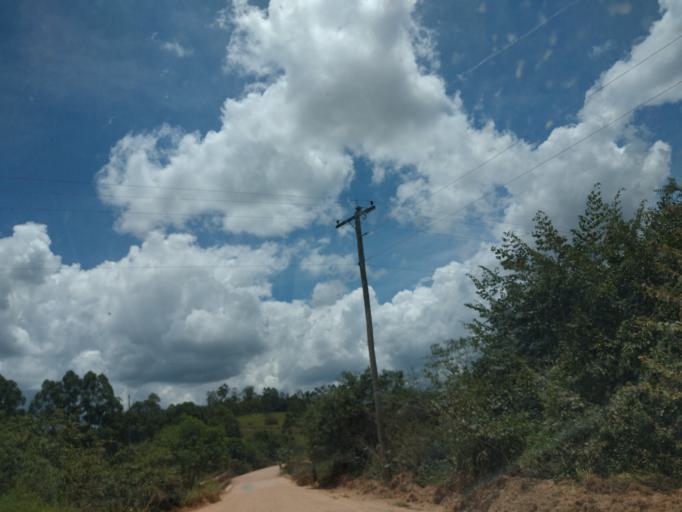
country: BR
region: Minas Gerais
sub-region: Sao Joao Del Rei
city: Sao Joao del Rei
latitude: -20.8997
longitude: -44.2999
